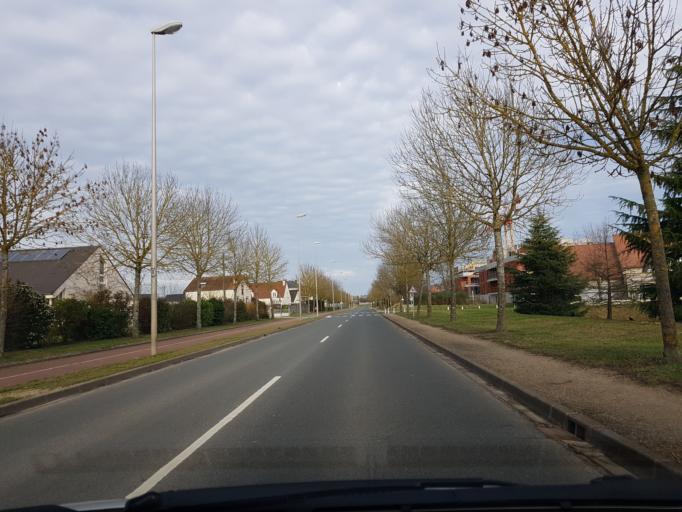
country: FR
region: Centre
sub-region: Departement du Loiret
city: Saint-Jean-le-Blanc
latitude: 47.8886
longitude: 1.9294
